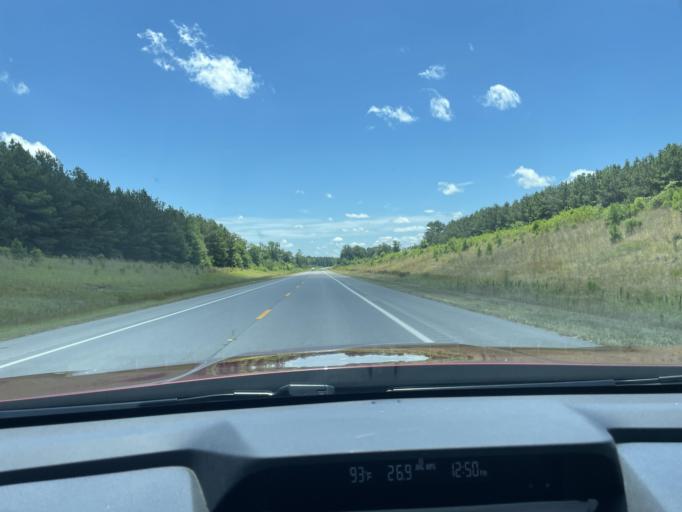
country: US
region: Arkansas
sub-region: Lincoln County
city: Star City
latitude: 33.9439
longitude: -91.8970
